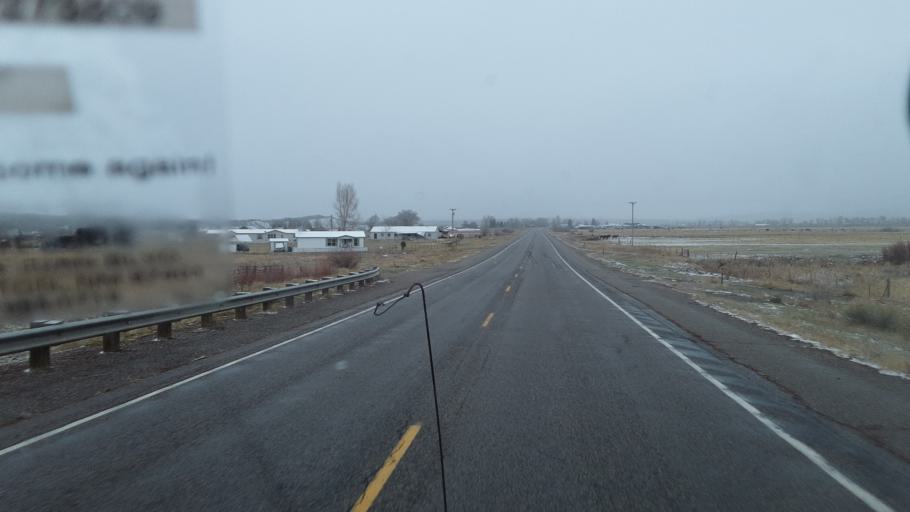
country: US
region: New Mexico
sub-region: Rio Arriba County
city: Tierra Amarilla
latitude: 36.7291
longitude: -106.5663
